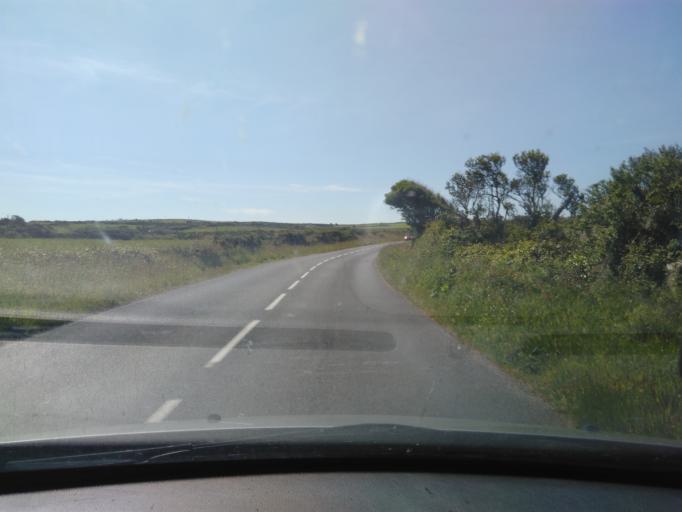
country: FR
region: Lower Normandy
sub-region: Departement de la Manche
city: Beaumont-Hague
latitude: 49.7056
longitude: -1.9309
